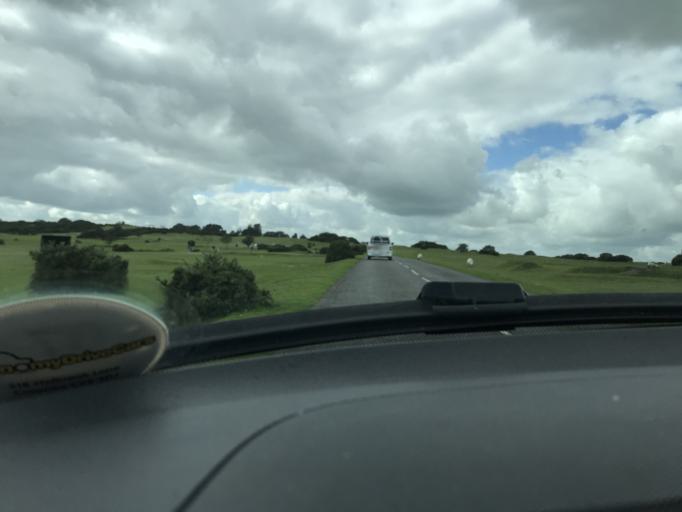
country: GB
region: England
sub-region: Devon
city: Tavistock
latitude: 50.5425
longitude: -4.1193
